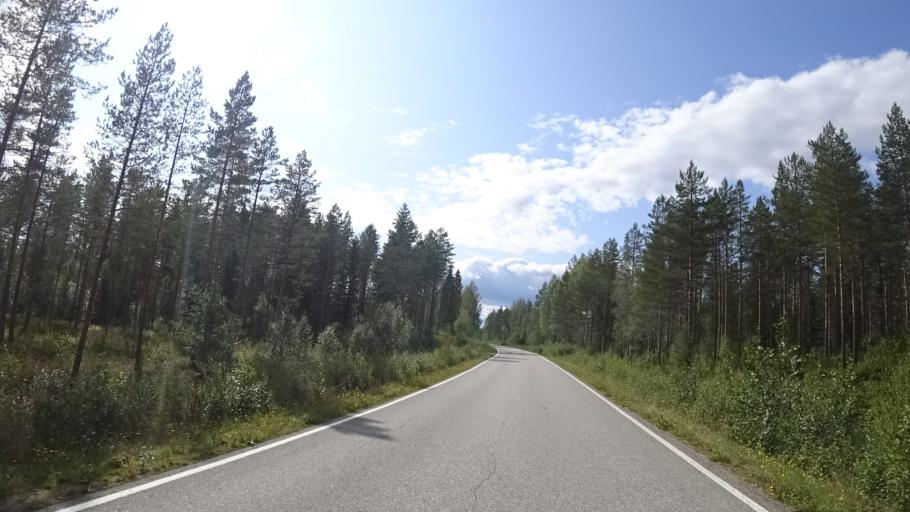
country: FI
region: North Karelia
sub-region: Joensuu
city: Ilomantsi
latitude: 62.4127
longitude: 30.9848
